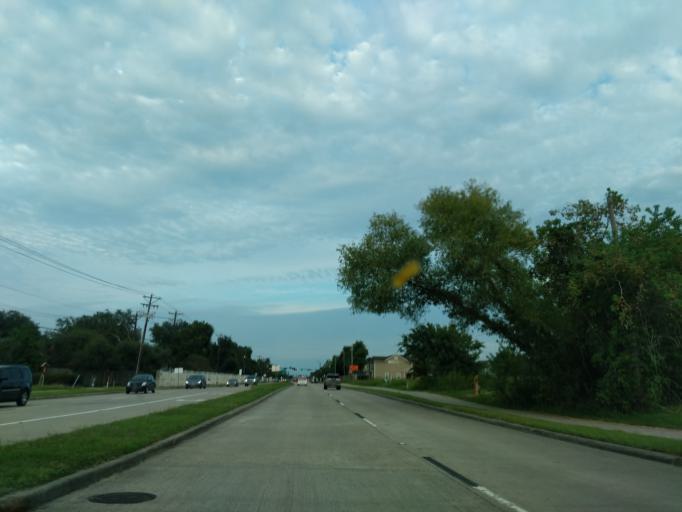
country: US
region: Texas
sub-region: Harris County
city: Nassau Bay
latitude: 29.5245
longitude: -95.0637
